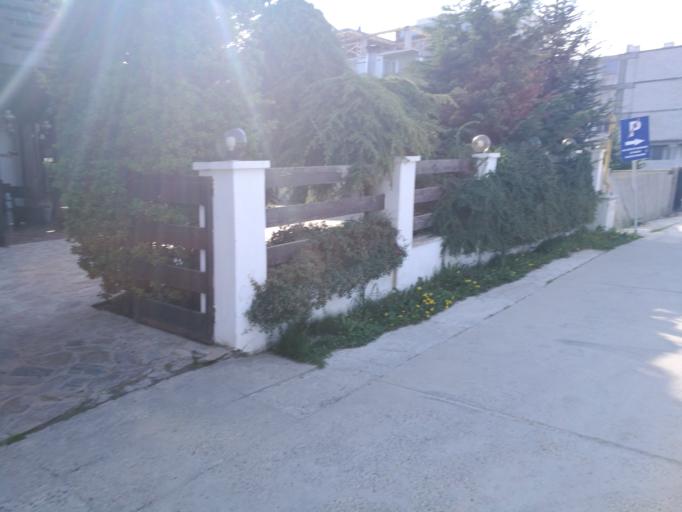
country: RO
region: Constanta
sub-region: Municipiul Constanta
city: Palazu Mare
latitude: 44.2143
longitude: 28.6212
